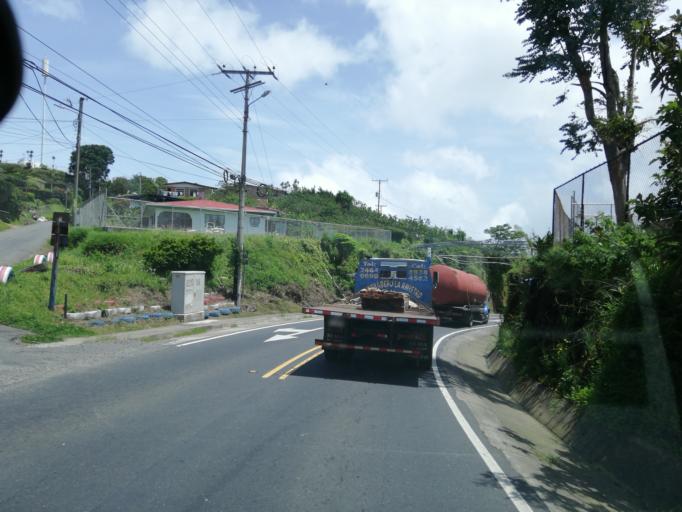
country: CR
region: Alajuela
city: Zarcero
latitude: 10.2182
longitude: -84.4025
